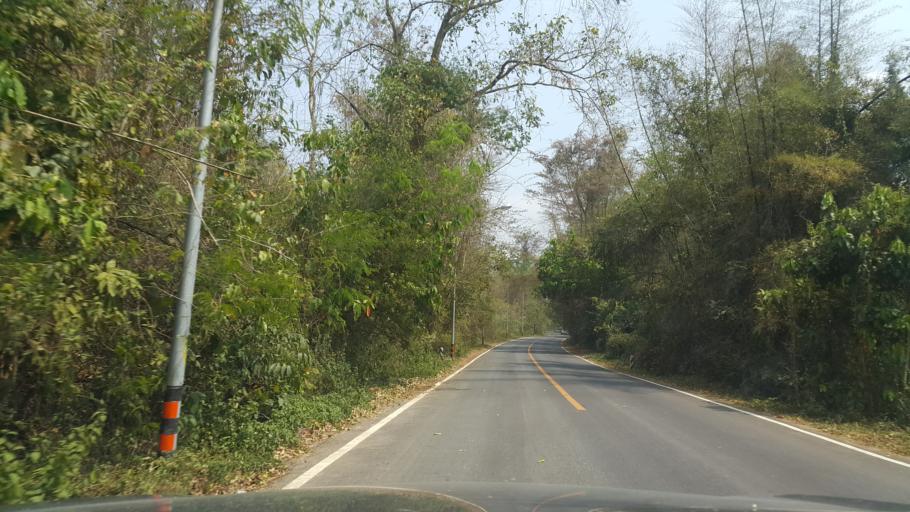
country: TH
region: Lamphun
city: Thung Hua Chang
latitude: 17.9034
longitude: 99.1263
